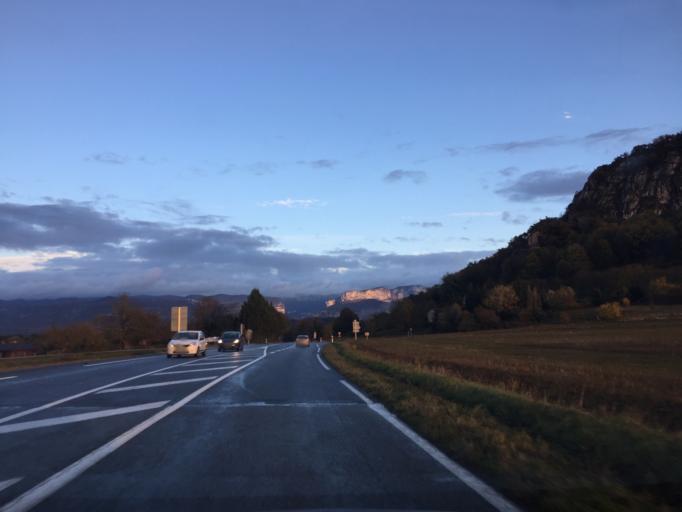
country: FR
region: Rhone-Alpes
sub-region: Departement de l'Isere
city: Saint-Hilaire-du-Rosier
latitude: 45.0661
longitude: 5.2304
